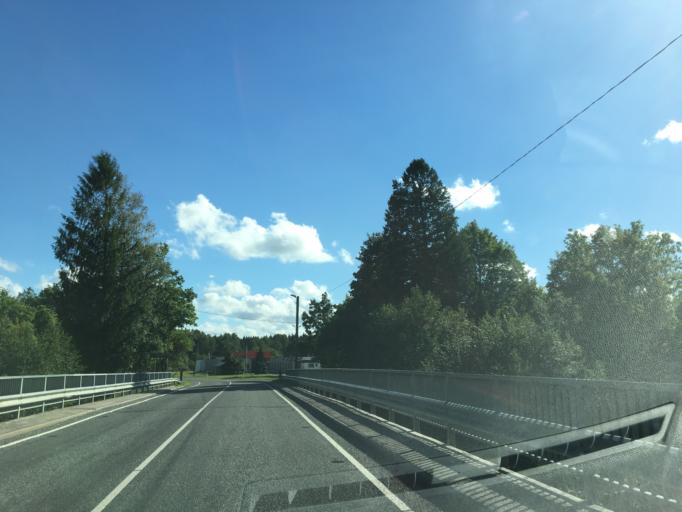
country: EE
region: Paernumaa
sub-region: Vaendra vald (alev)
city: Vandra
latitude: 58.6171
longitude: 25.1031
